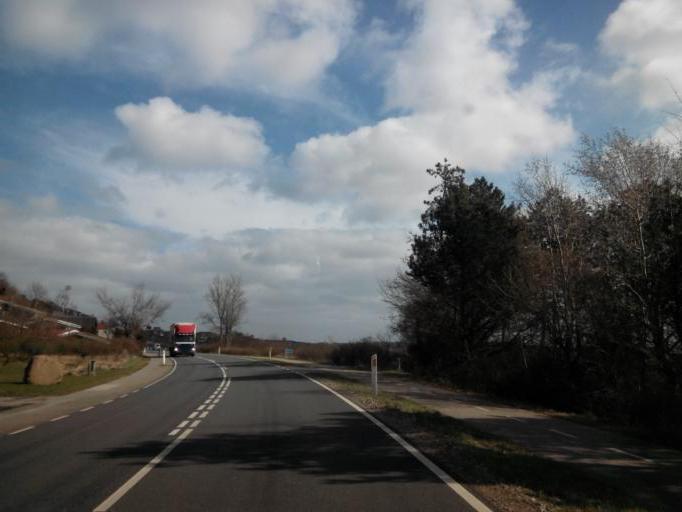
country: DK
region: Central Jutland
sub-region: Syddjurs Kommune
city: Ebeltoft
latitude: 56.2273
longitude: 10.6307
